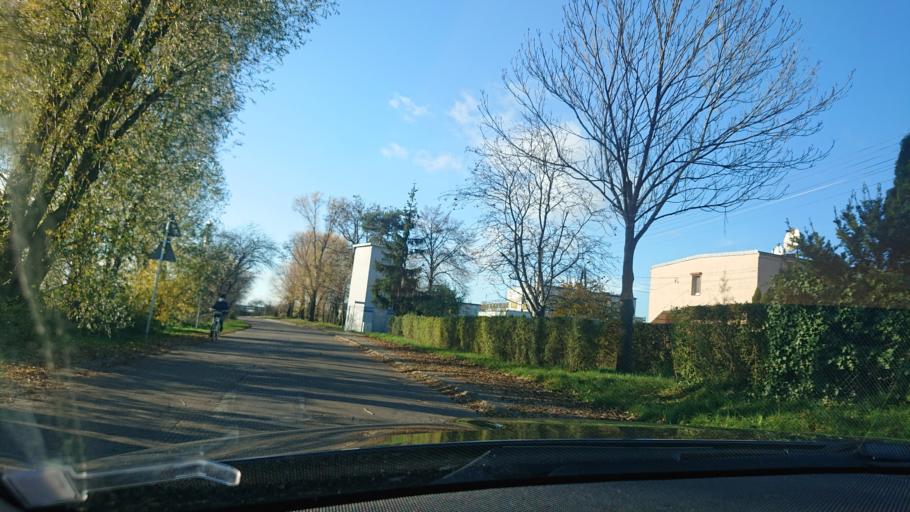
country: PL
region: Greater Poland Voivodeship
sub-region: Powiat gnieznienski
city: Gniezno
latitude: 52.5265
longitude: 17.5807
